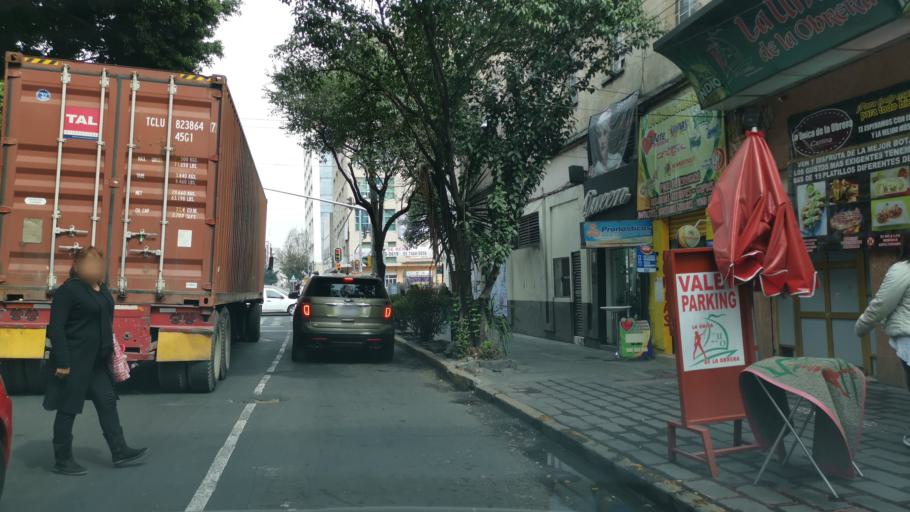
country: MX
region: Mexico City
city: Mexico City
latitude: 19.4237
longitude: -99.1376
